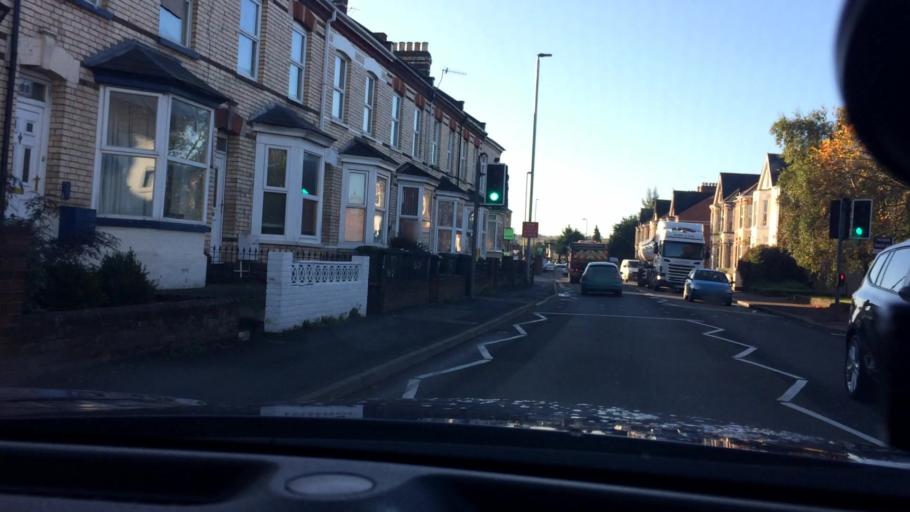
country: GB
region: England
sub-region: Devon
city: Exeter
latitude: 50.7111
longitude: -3.5377
